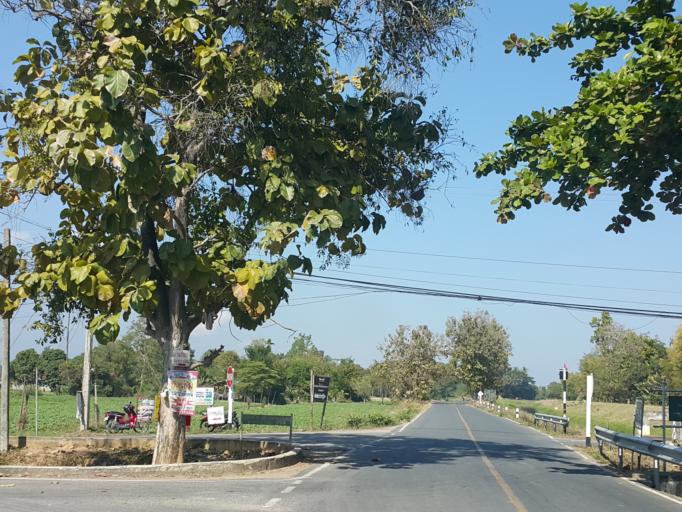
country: TH
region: Chiang Mai
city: San Sai
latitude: 18.9482
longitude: 98.9911
